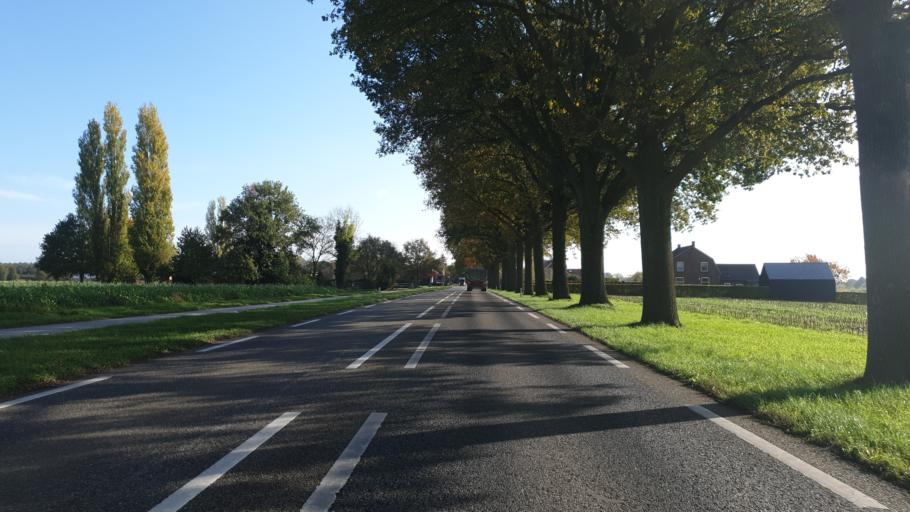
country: NL
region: North Brabant
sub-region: Gemeente Boxmeer
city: Boxmeer
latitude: 51.6293
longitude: 6.0179
